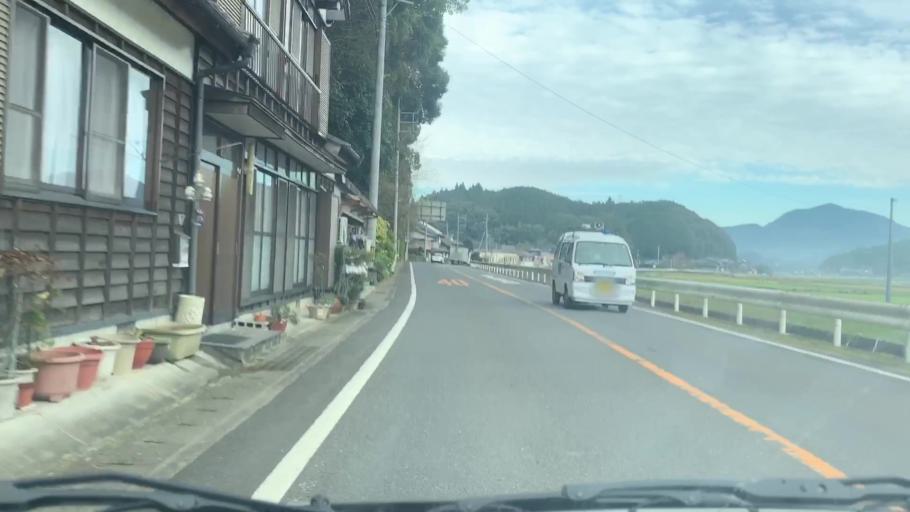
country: JP
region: Saga Prefecture
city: Takeocho-takeo
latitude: 33.2273
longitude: 129.9638
